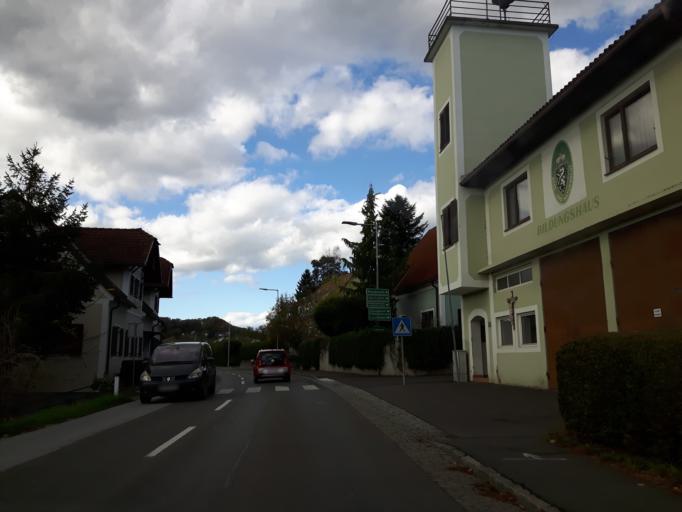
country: AT
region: Styria
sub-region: Politischer Bezirk Suedoststeiermark
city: Sankt Stefan im Rosental
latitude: 46.9043
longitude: 15.7092
